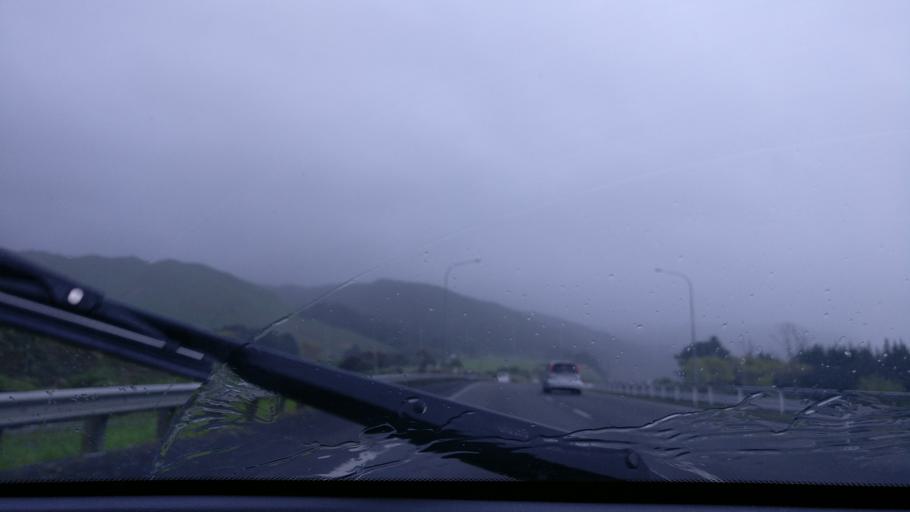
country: NZ
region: Wellington
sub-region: Kapiti Coast District
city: Paraparaumu
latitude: -40.9698
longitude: 174.9838
